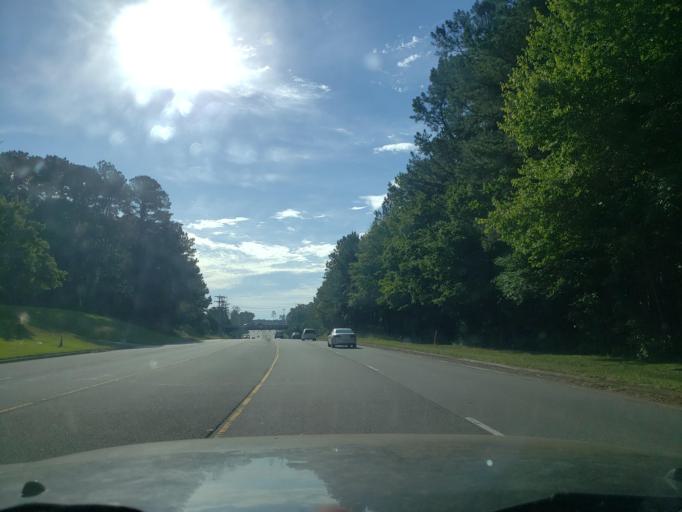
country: US
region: North Carolina
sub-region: Durham County
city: Durham
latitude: 35.9397
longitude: -78.8628
